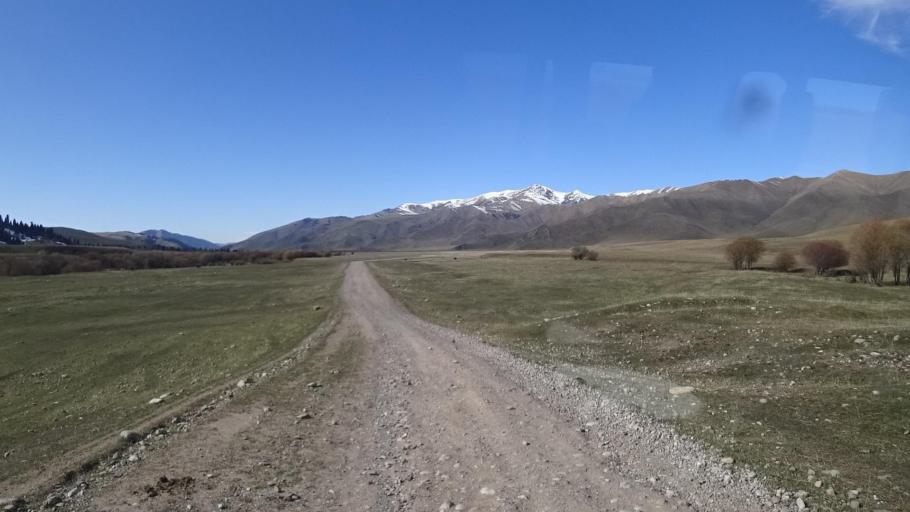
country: KZ
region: Almaty Oblysy
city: Kegen
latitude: 42.7370
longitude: 79.0139
